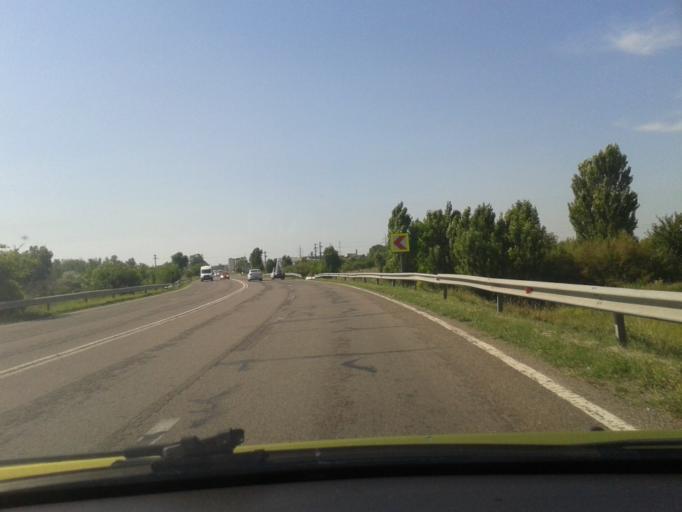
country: RO
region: Constanta
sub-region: Municipiul Mangalia
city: Mangalia
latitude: 43.8383
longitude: 28.5760
